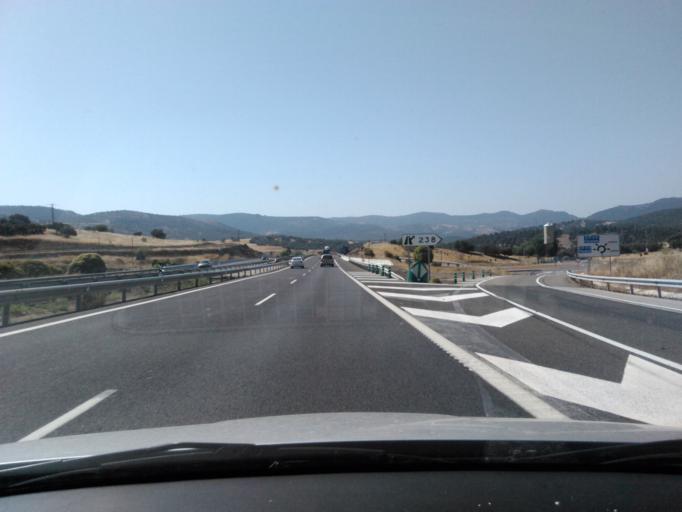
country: ES
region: Castille-La Mancha
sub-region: Provincia de Ciudad Real
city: Viso del Marques
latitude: 38.4598
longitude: -3.5005
